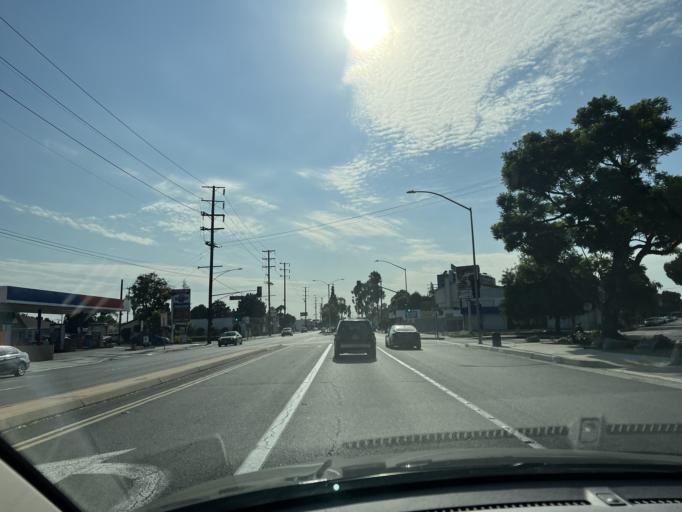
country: US
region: California
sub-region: Los Angeles County
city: Norwalk
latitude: 33.9023
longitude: -118.0763
